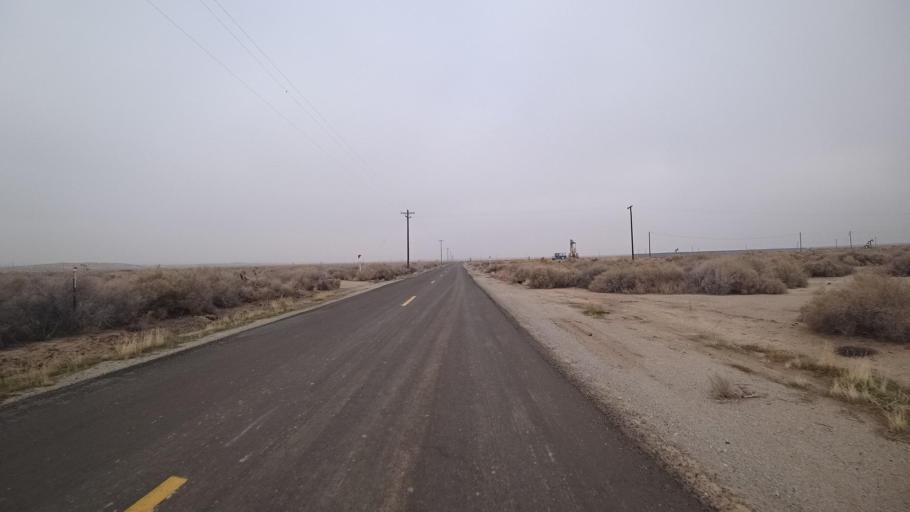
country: US
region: California
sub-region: Kern County
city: Maricopa
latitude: 35.0710
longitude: -119.3492
